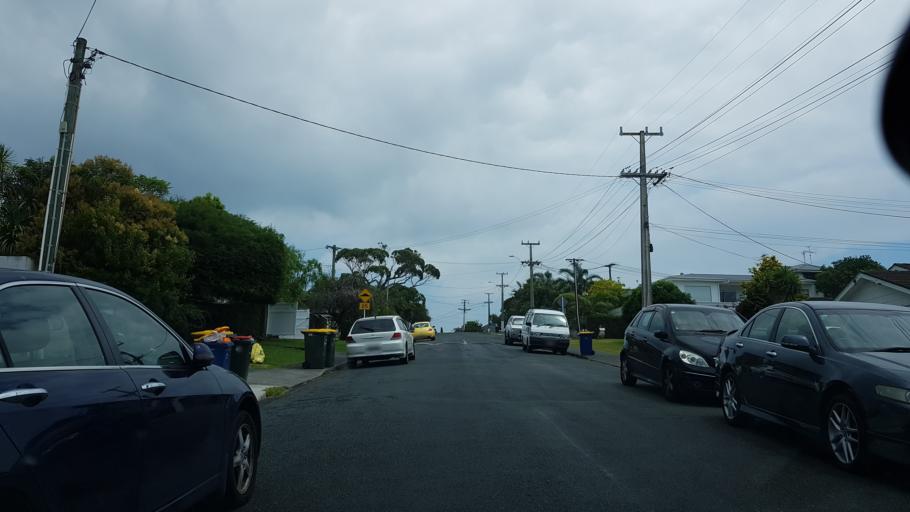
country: NZ
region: Auckland
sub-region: Auckland
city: North Shore
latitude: -36.7982
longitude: 174.7737
